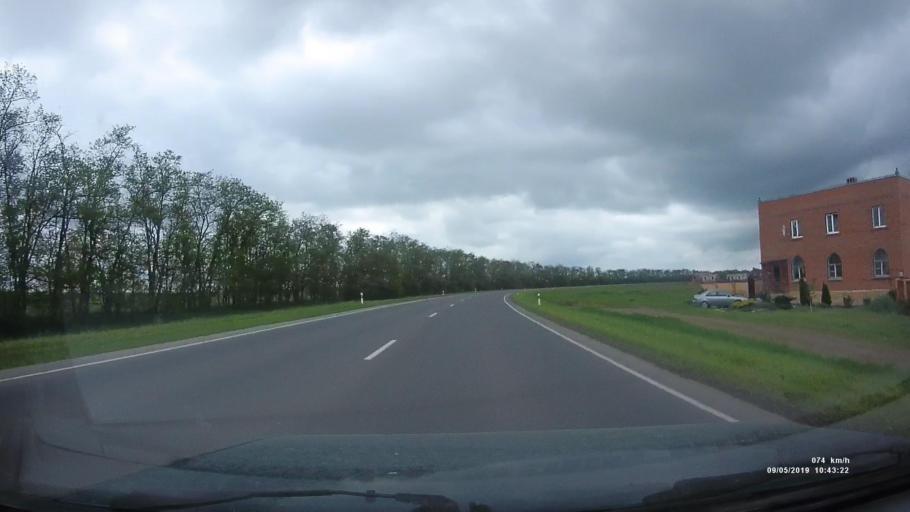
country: RU
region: Rostov
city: Peshkovo
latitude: 47.0088
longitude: 39.4037
